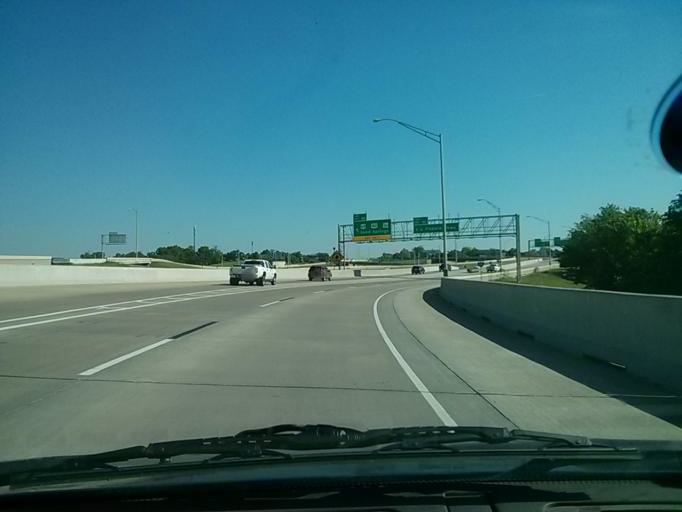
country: US
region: Oklahoma
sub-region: Tulsa County
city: Tulsa
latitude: 36.1563
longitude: -96.0014
